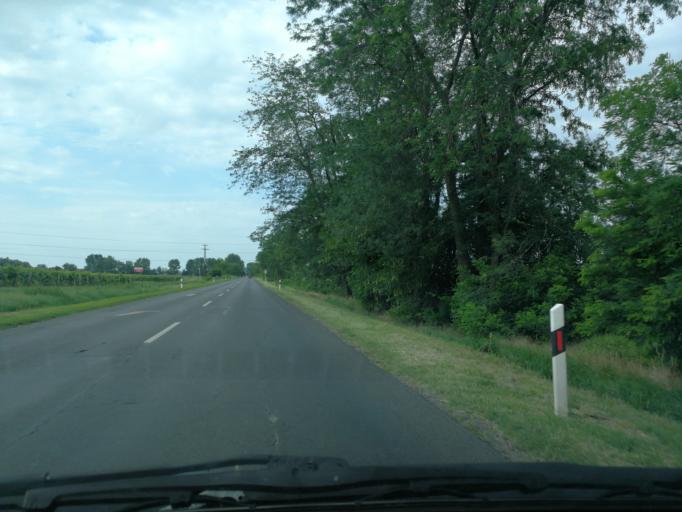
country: HU
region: Bacs-Kiskun
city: Ersekcsanad
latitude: 46.2245
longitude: 18.9676
